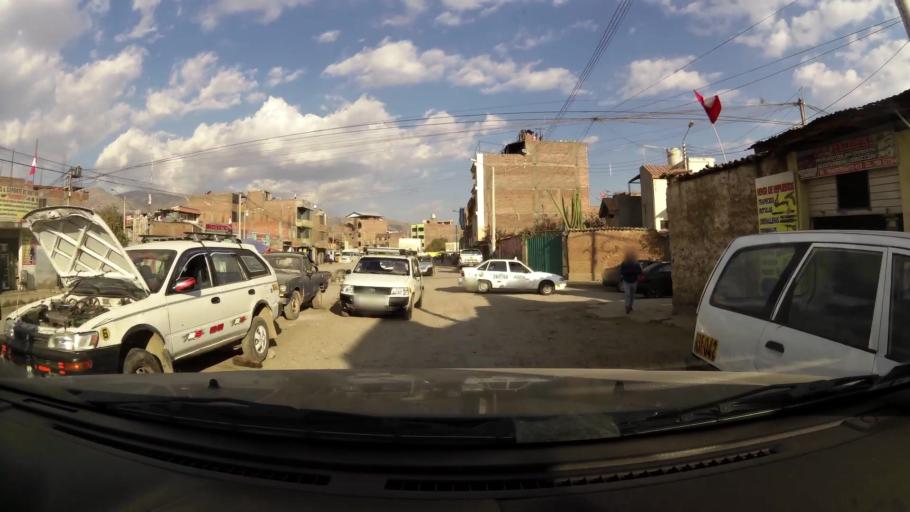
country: PE
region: Junin
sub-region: Provincia de Huancayo
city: El Tambo
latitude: -12.0520
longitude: -75.2175
